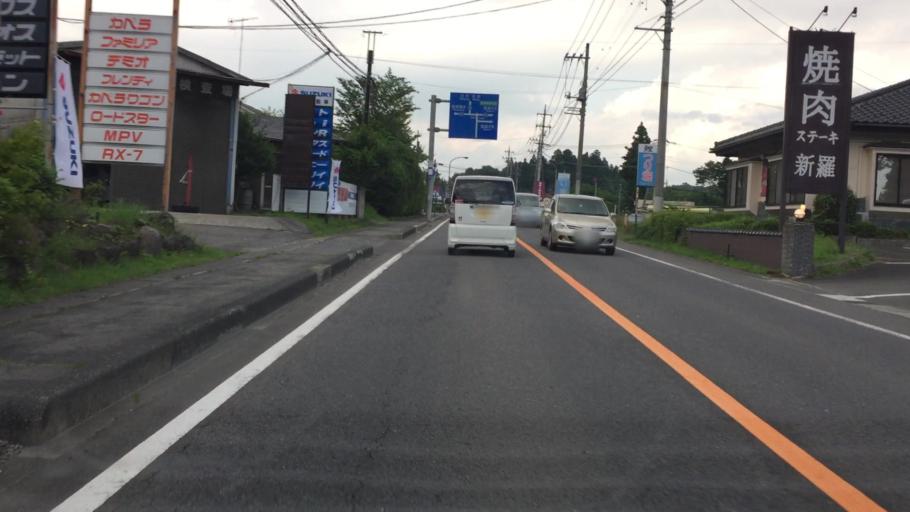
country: JP
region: Tochigi
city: Kuroiso
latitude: 37.0544
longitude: 140.0357
